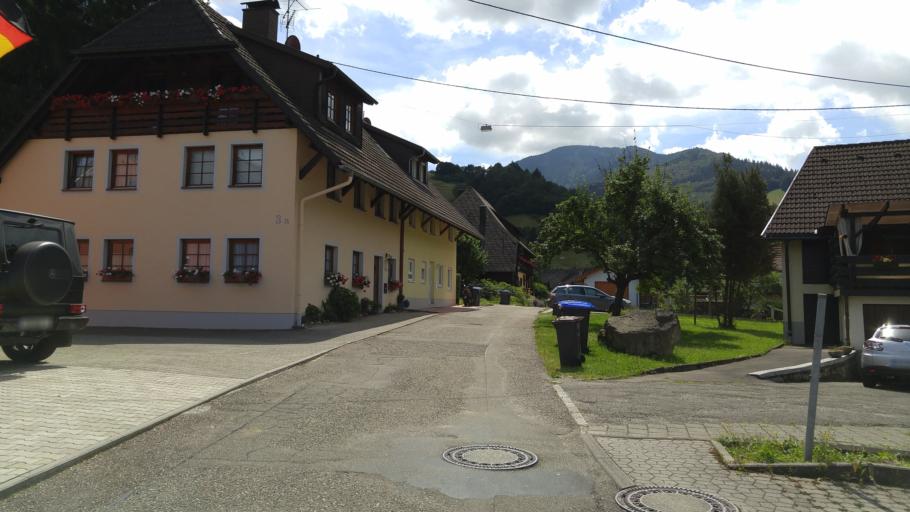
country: DE
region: Baden-Wuerttemberg
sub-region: Freiburg Region
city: Muenstertal/Schwarzwald
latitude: 47.8500
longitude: 7.7898
